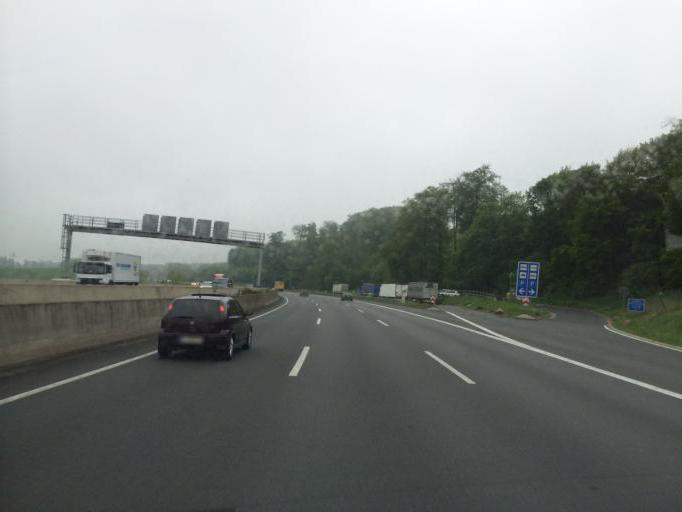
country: DE
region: Lower Saxony
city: Buchholz
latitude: 52.2166
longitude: 9.1651
